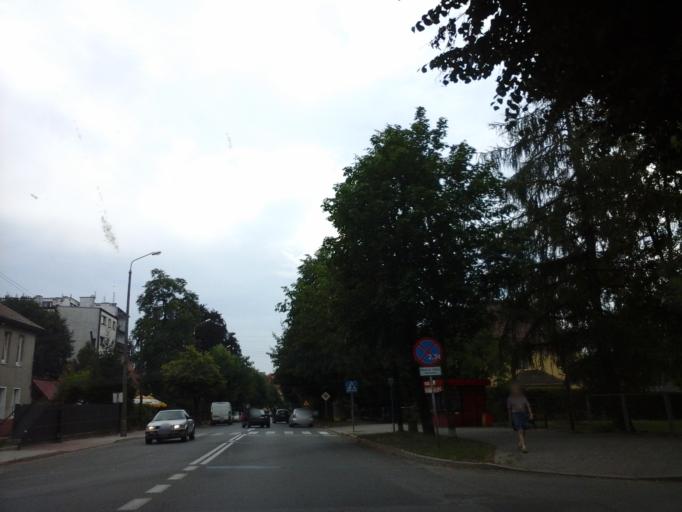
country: PL
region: Lower Silesian Voivodeship
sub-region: Powiat zabkowicki
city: Zabkowice Slaskie
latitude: 50.5991
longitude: 16.8188
